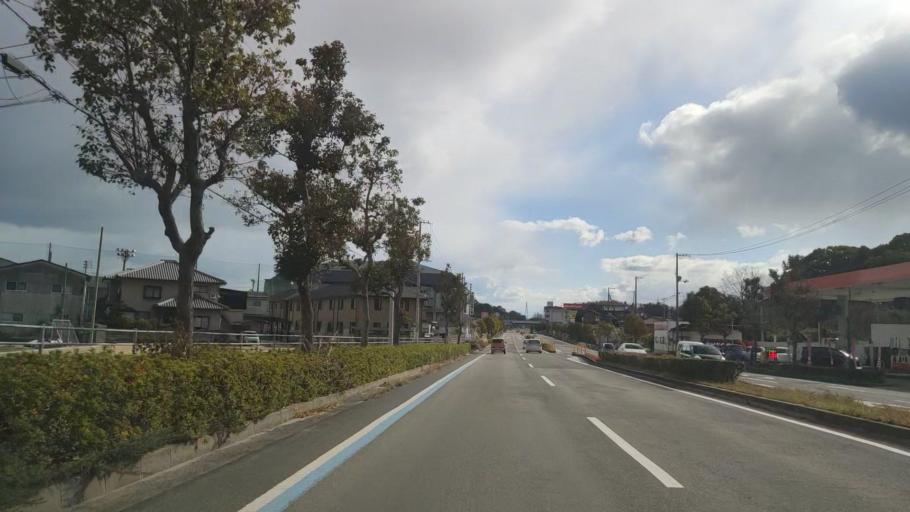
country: JP
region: Ehime
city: Hojo
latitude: 34.0603
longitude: 132.9661
